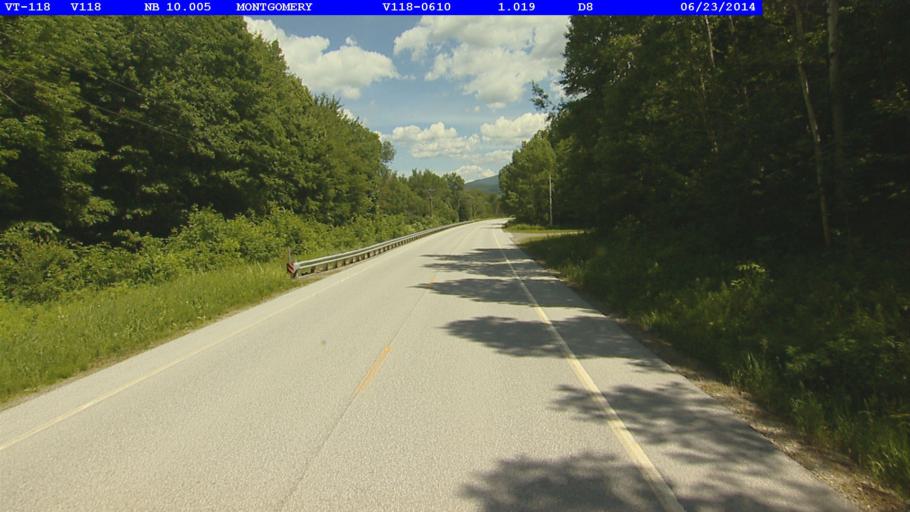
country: US
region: Vermont
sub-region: Lamoille County
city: Johnson
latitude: 44.8141
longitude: -72.6173
